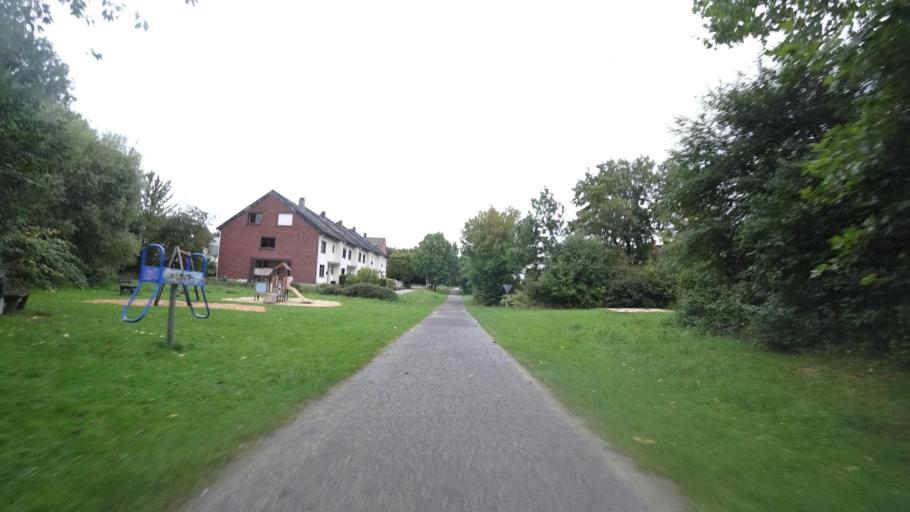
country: DE
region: North Rhine-Westphalia
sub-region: Regierungsbezirk Detmold
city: Bielefeld
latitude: 52.0439
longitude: 8.5520
